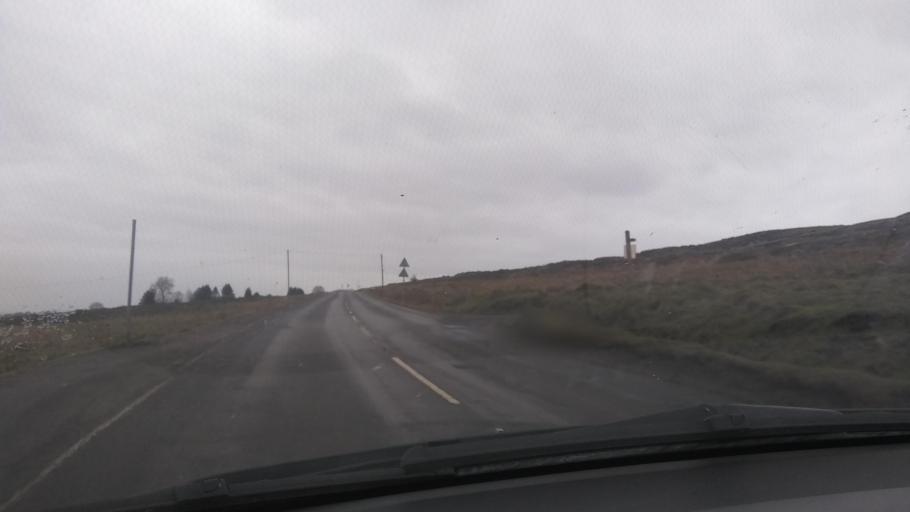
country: GB
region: England
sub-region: Worcestershire
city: Tenbury Wells
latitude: 52.3814
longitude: -2.5675
